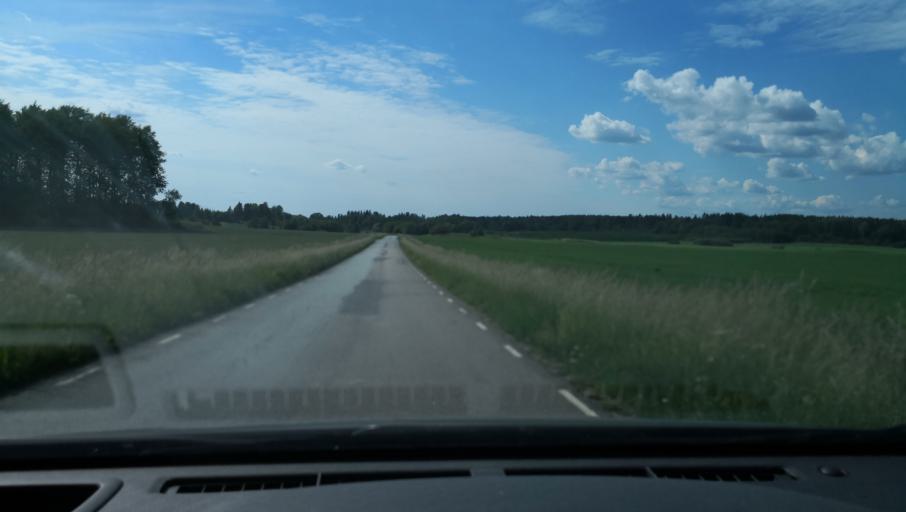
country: SE
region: Uppsala
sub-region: Enkopings Kommun
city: Orsundsbro
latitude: 59.8134
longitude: 17.3789
